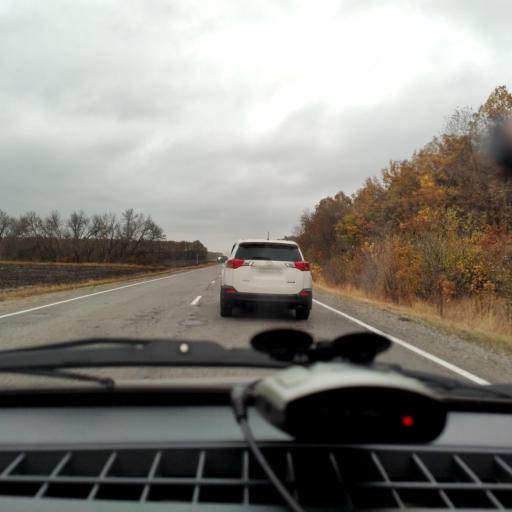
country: RU
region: Voronezj
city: Shilovo
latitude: 51.4161
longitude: 39.0060
